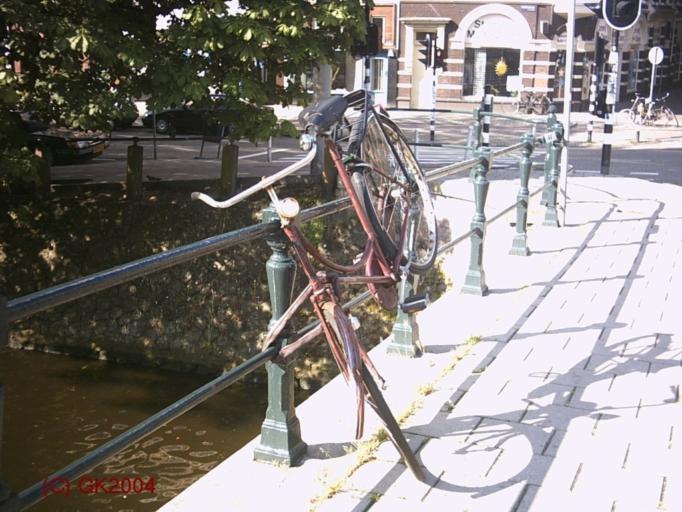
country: NL
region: North Holland
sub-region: Gemeente Amsterdam
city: Amsterdam
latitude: 52.3718
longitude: 4.8959
